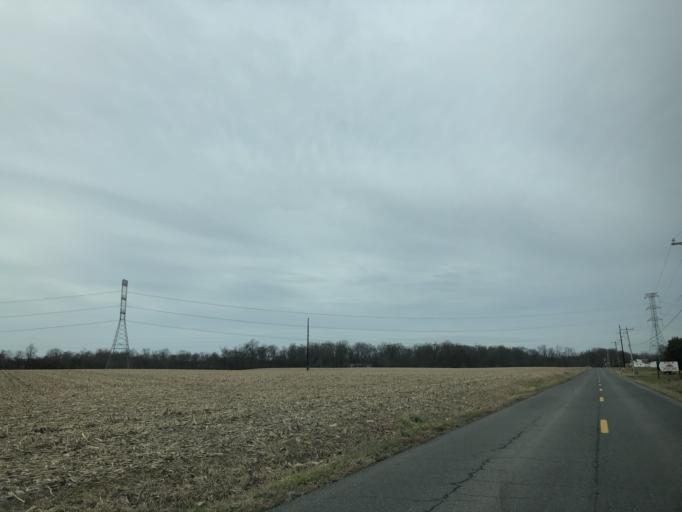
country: US
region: Delaware
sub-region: New Castle County
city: Middletown
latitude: 39.4371
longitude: -75.7607
